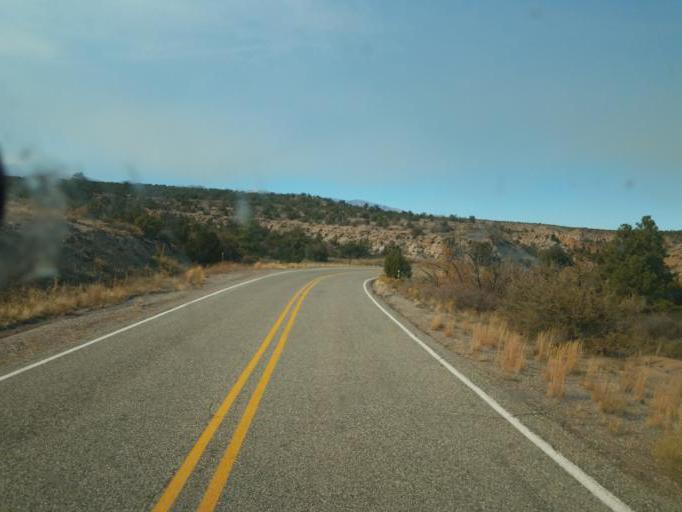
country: US
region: New Mexico
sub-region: Los Alamos County
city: White Rock
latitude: 35.7988
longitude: -106.2456
